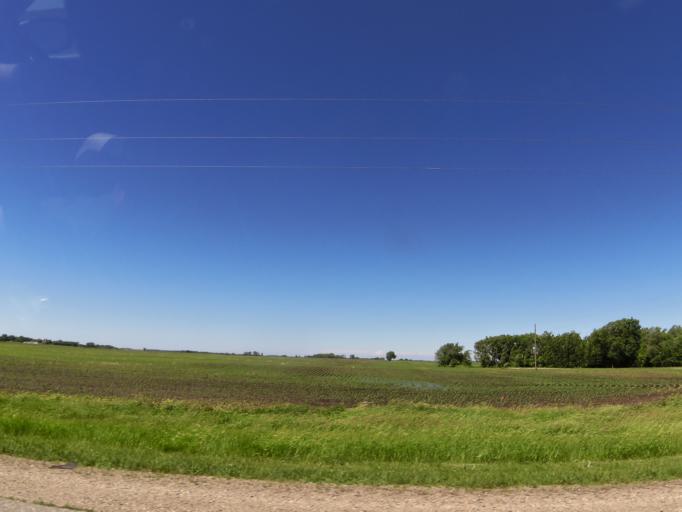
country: US
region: Minnesota
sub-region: Mahnomen County
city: Mahnomen
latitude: 47.2671
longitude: -95.9334
